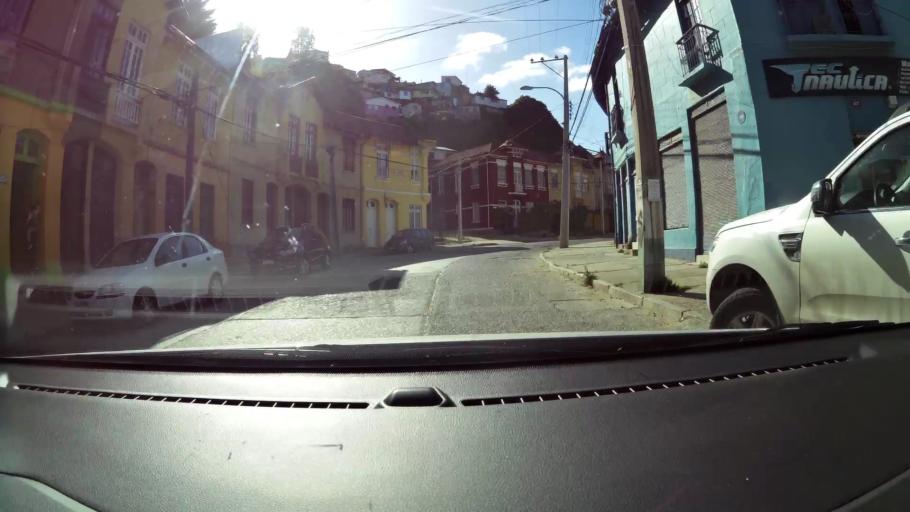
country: CL
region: Valparaiso
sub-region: Provincia de Valparaiso
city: Valparaiso
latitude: -33.0565
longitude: -71.6008
